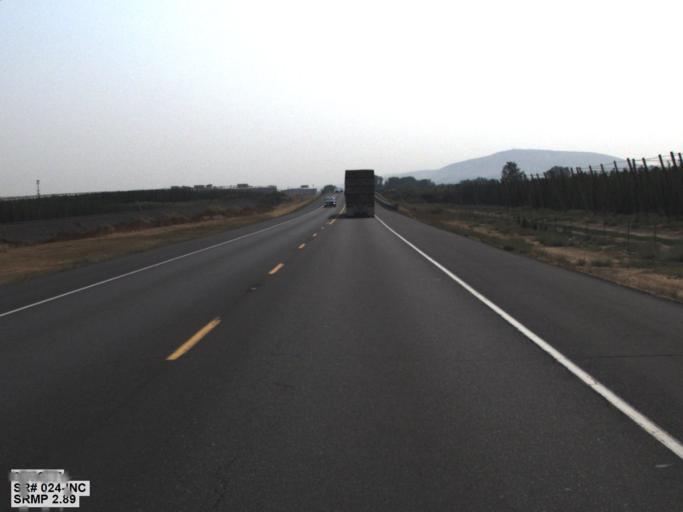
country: US
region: Washington
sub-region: Yakima County
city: Terrace Heights
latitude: 46.5688
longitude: -120.4205
